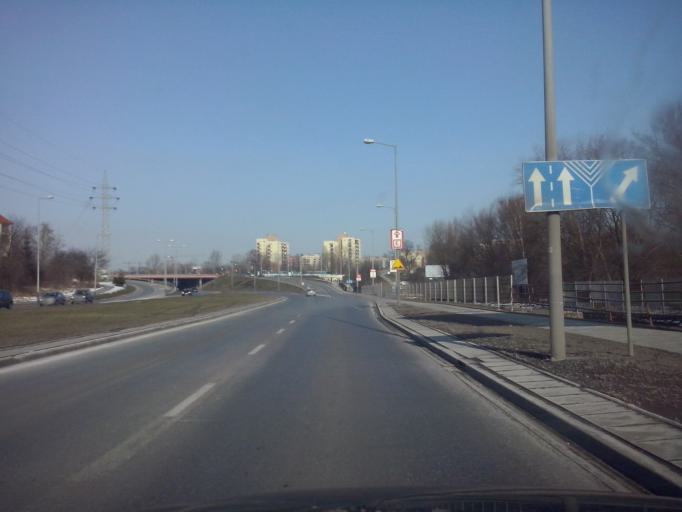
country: PL
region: Lesser Poland Voivodeship
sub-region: Krakow
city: Krakow
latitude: 50.0711
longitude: 20.0050
